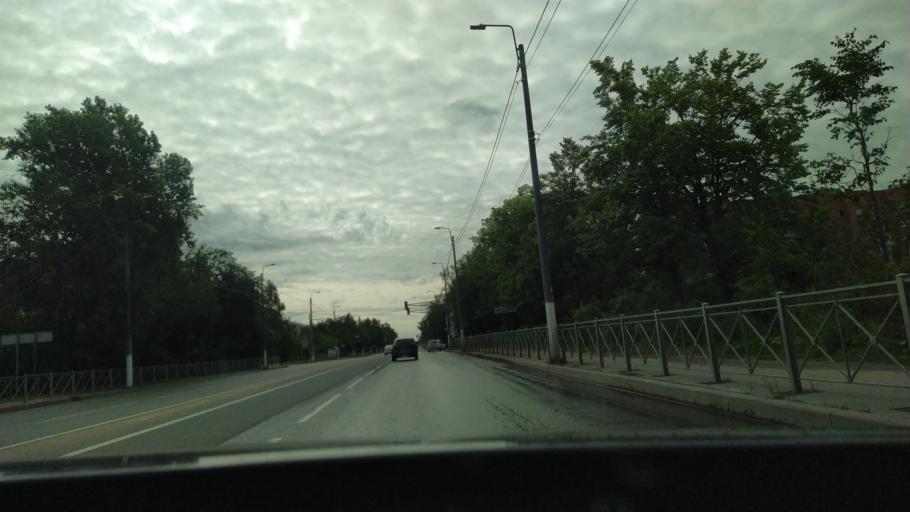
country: RU
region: Leningrad
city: Tosno
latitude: 59.5485
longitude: 30.8632
